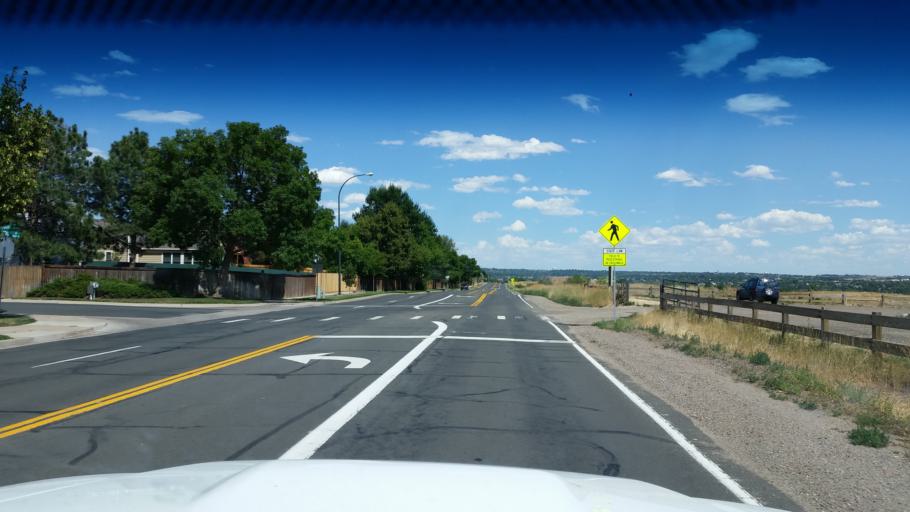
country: US
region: Colorado
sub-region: Broomfield County
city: Broomfield
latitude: 39.8782
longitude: -105.1224
